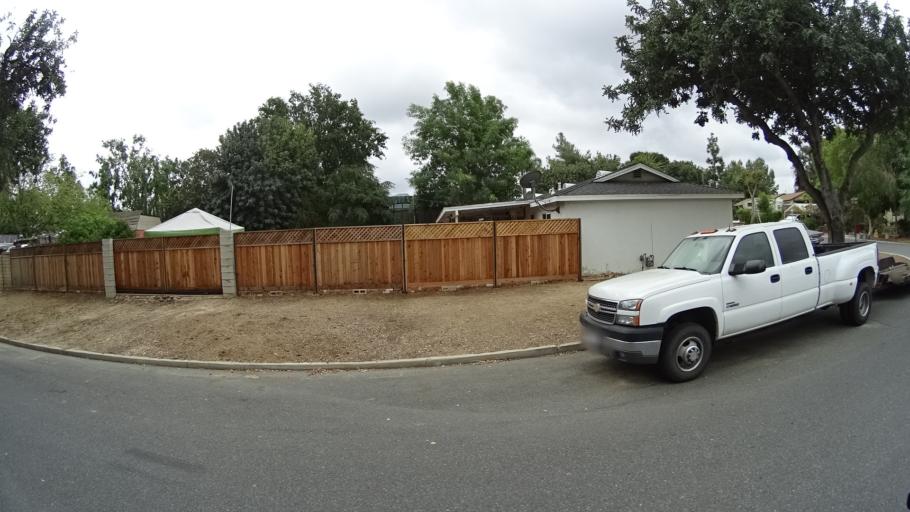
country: US
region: California
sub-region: Ventura County
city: Thousand Oaks
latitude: 34.2127
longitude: -118.8612
